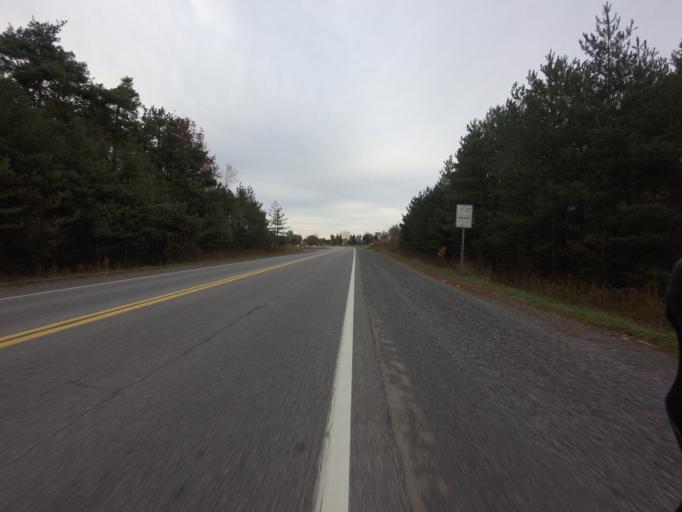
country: CA
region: Ontario
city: Bells Corners
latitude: 45.1551
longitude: -75.7089
